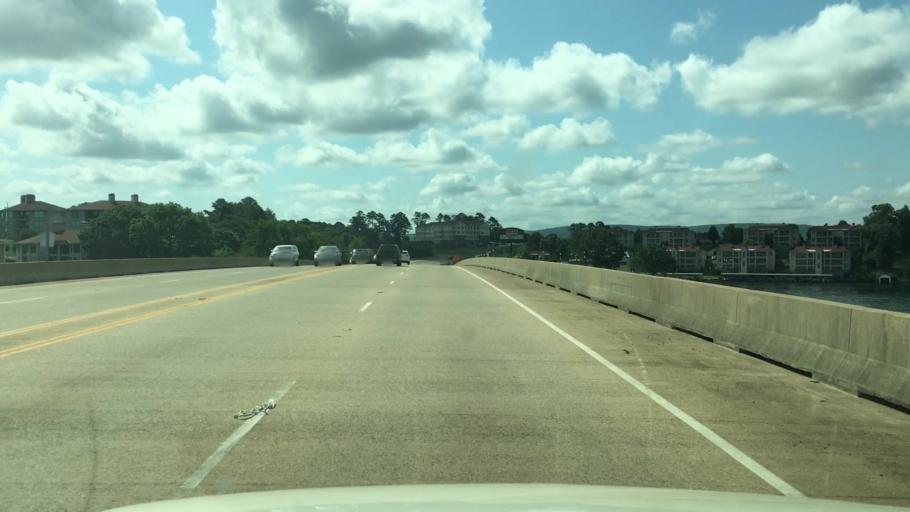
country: US
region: Arkansas
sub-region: Garland County
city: Lake Hamilton
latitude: 34.4331
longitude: -93.0875
